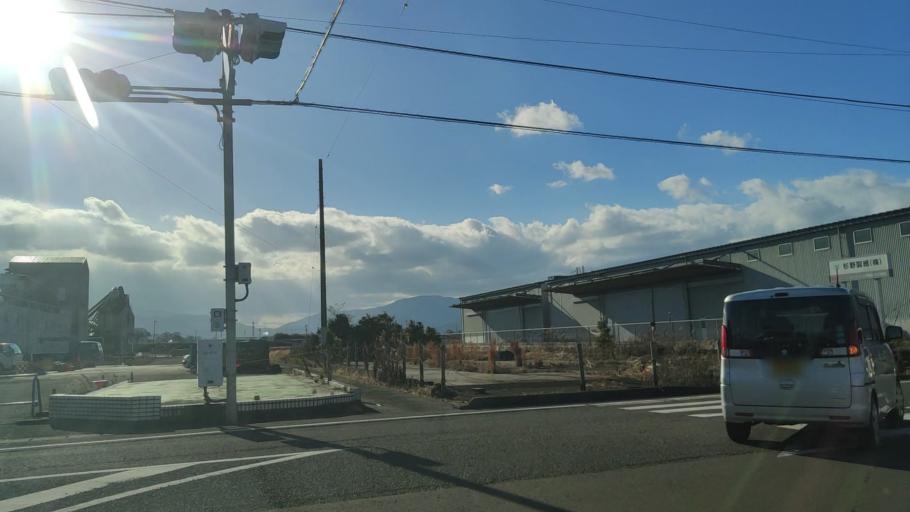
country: JP
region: Ehime
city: Saijo
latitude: 33.9104
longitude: 133.1113
